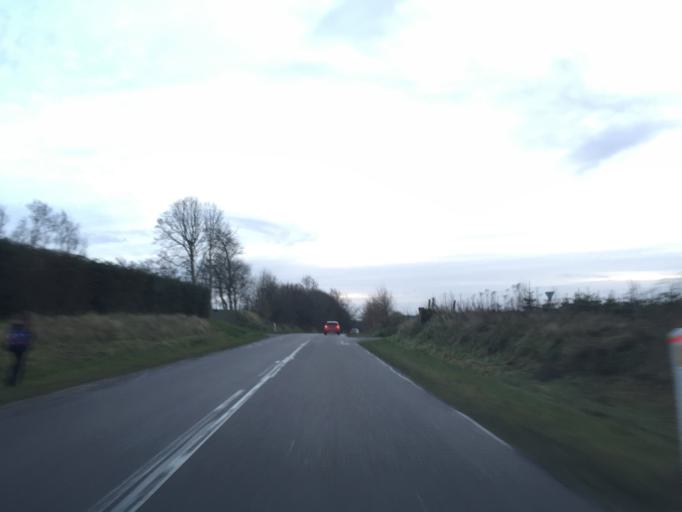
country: DK
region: Central Jutland
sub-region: Viborg Kommune
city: Bjerringbro
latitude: 56.3503
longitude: 9.6592
